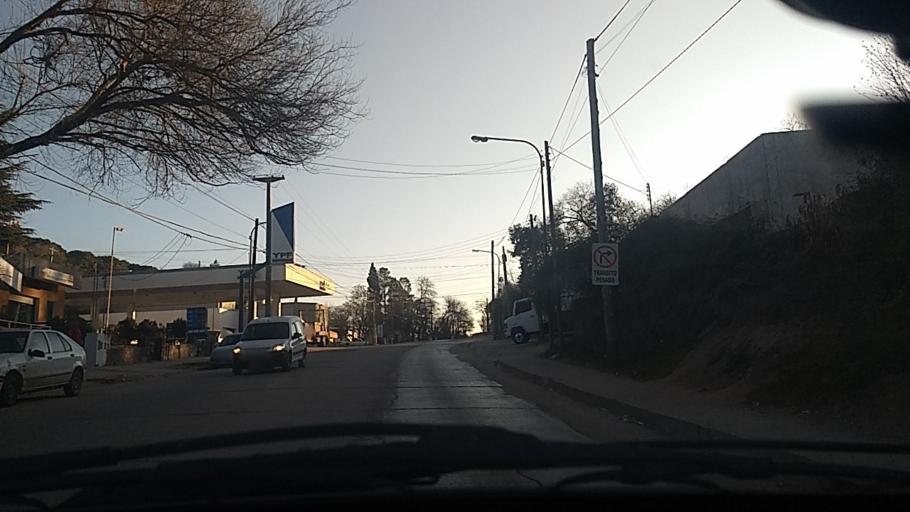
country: AR
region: Cordoba
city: Salsipuedes
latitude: -31.1378
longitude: -64.2967
